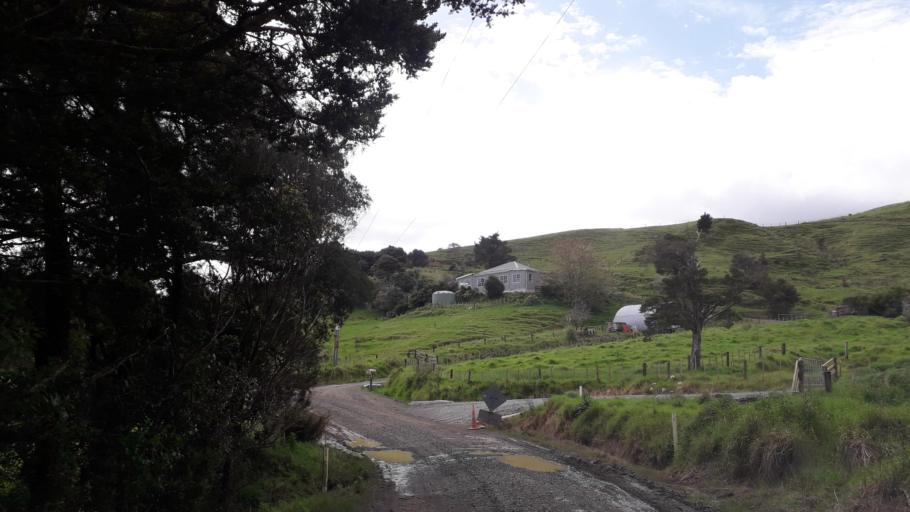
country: NZ
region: Northland
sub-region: Far North District
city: Kaitaia
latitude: -35.2296
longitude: 173.2651
